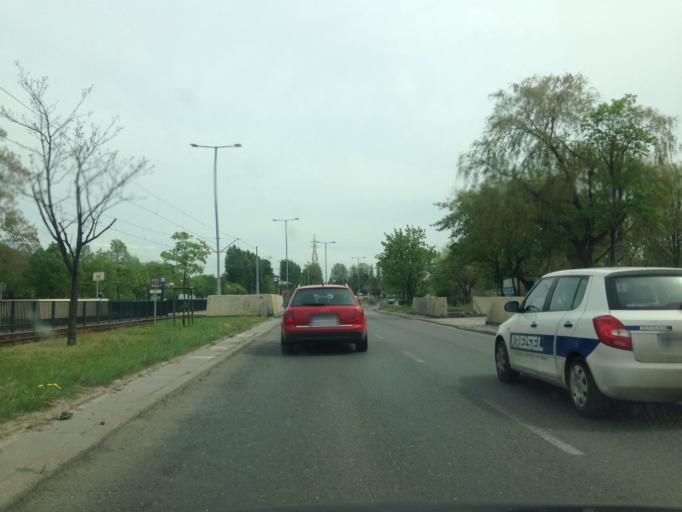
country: PL
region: Pomeranian Voivodeship
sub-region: Gdansk
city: Gdansk
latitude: 54.3924
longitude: 18.6052
